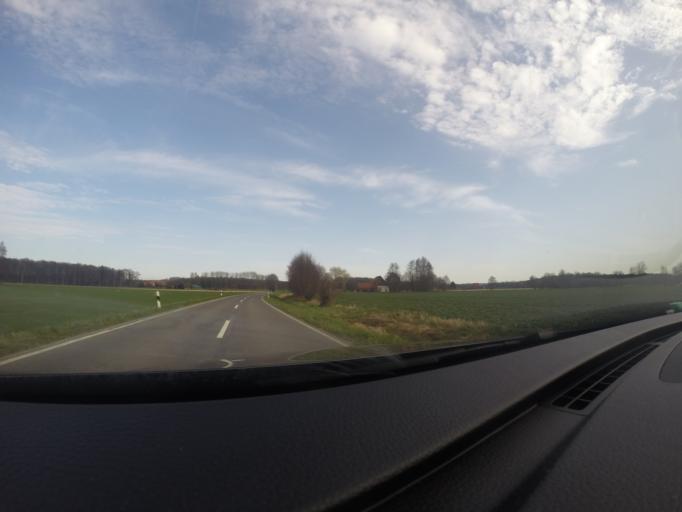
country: DE
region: North Rhine-Westphalia
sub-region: Regierungsbezirk Munster
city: Schoppingen
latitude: 52.0447
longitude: 7.2351
